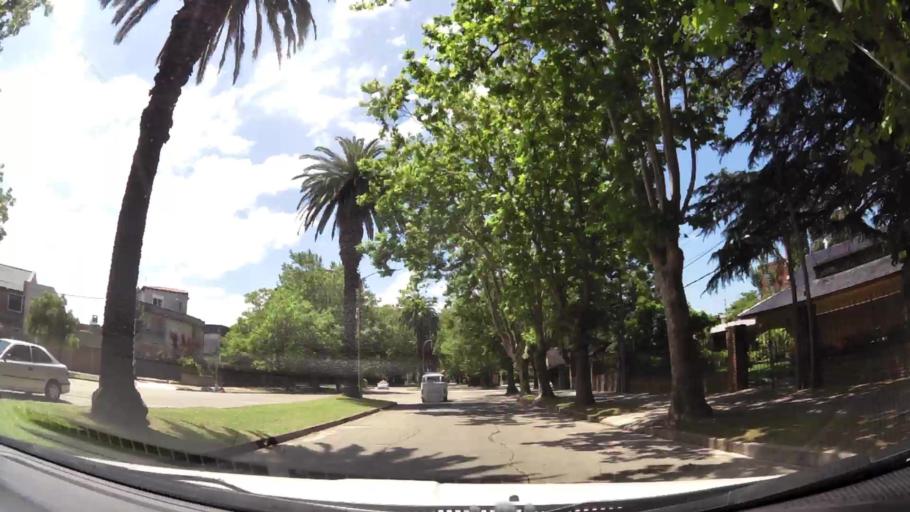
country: UY
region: Montevideo
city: Montevideo
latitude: -34.8652
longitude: -56.1975
